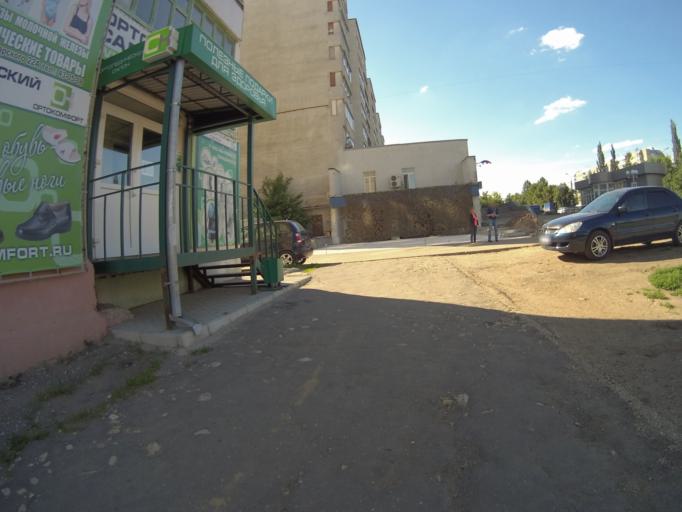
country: RU
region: Vladimir
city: Kommunar
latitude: 56.1621
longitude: 40.4709
